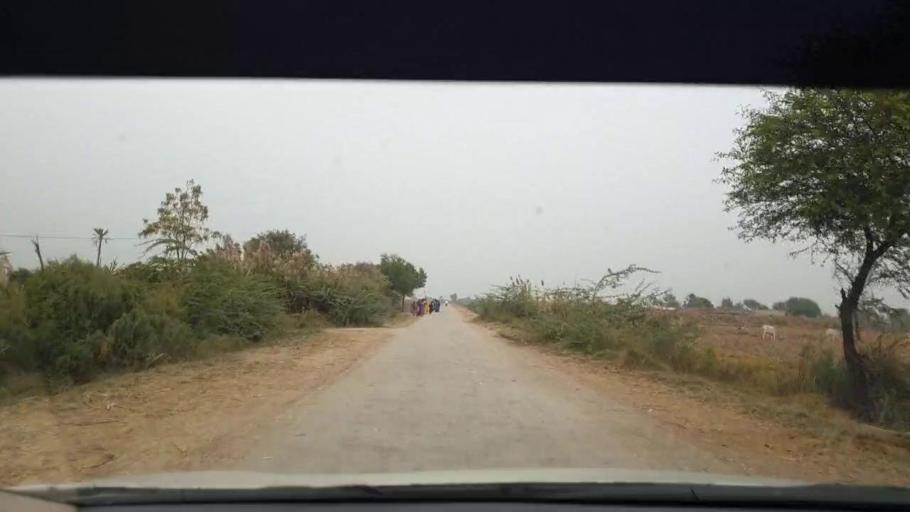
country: PK
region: Sindh
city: Berani
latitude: 25.8471
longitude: 68.8653
